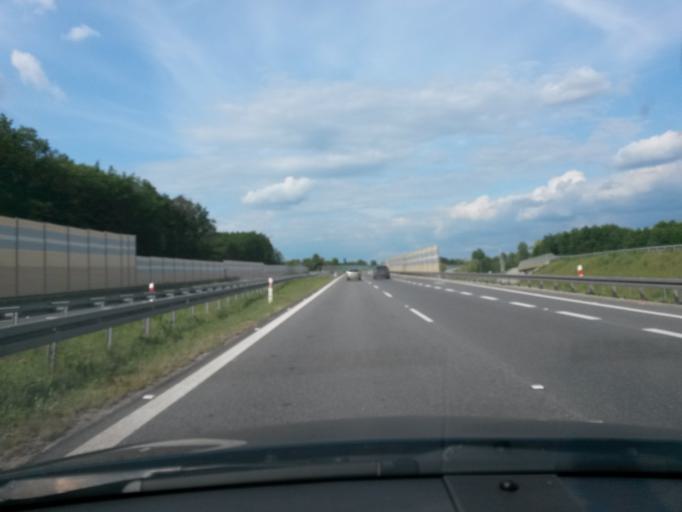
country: PL
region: Masovian Voivodeship
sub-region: Powiat zyrardowski
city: Radziejowice
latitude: 51.9986
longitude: 20.5541
